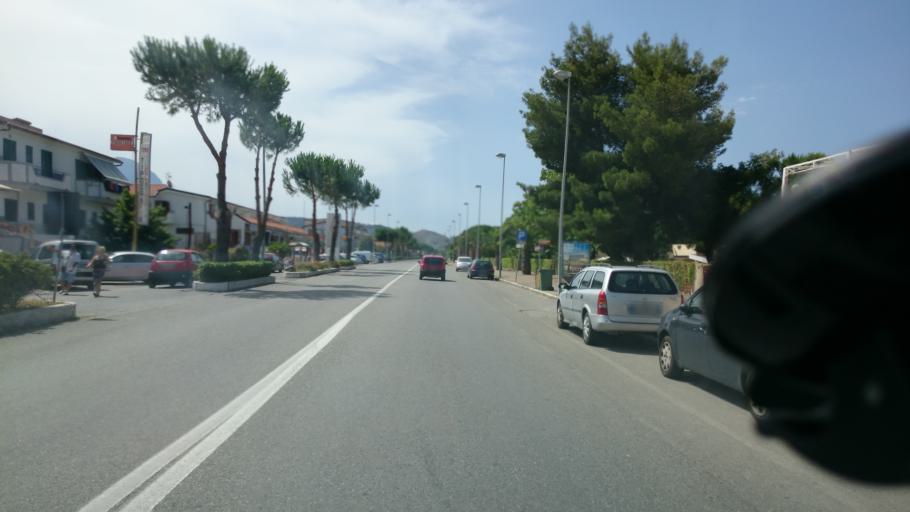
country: IT
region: Calabria
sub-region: Provincia di Cosenza
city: Marcellina
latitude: 39.7529
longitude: 15.8048
